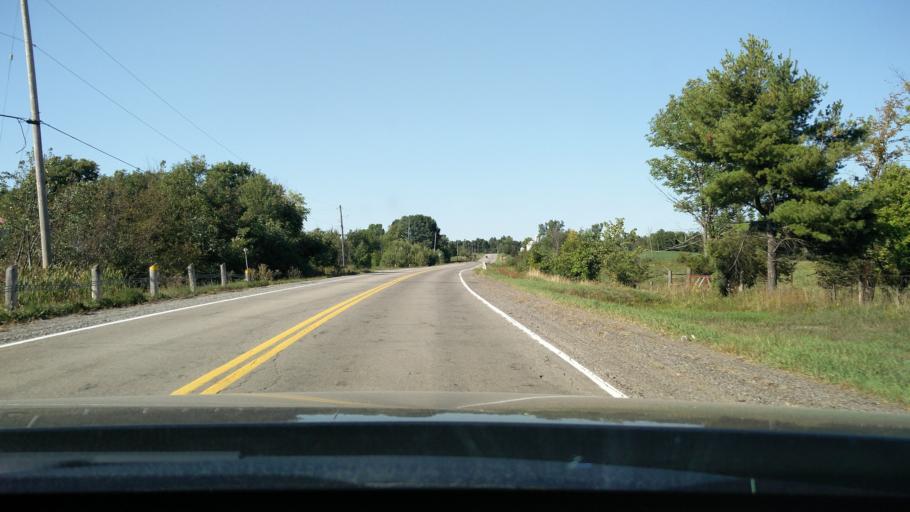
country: CA
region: Ontario
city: Perth
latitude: 44.6968
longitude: -76.4012
